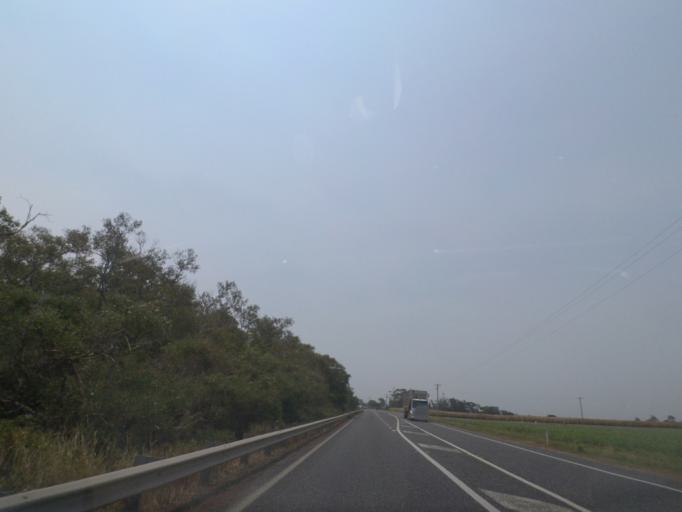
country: AU
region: New South Wales
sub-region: Ballina
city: Ballina
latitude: -28.9692
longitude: 153.4615
